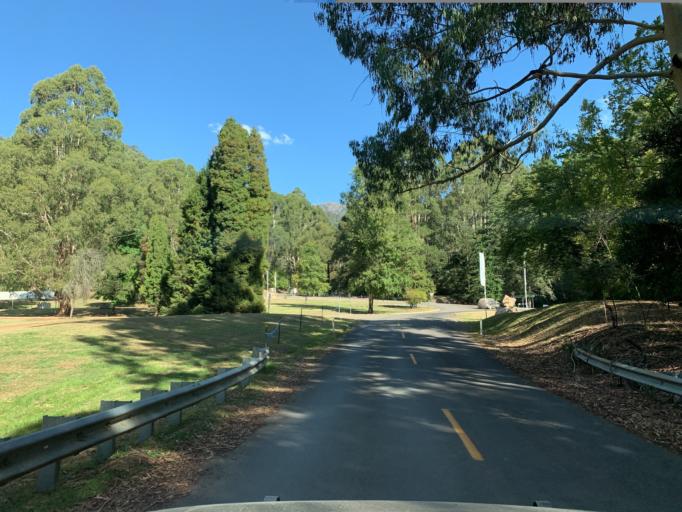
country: AU
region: Victoria
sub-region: Mansfield
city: Mansfield
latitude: -37.1096
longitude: 146.3997
